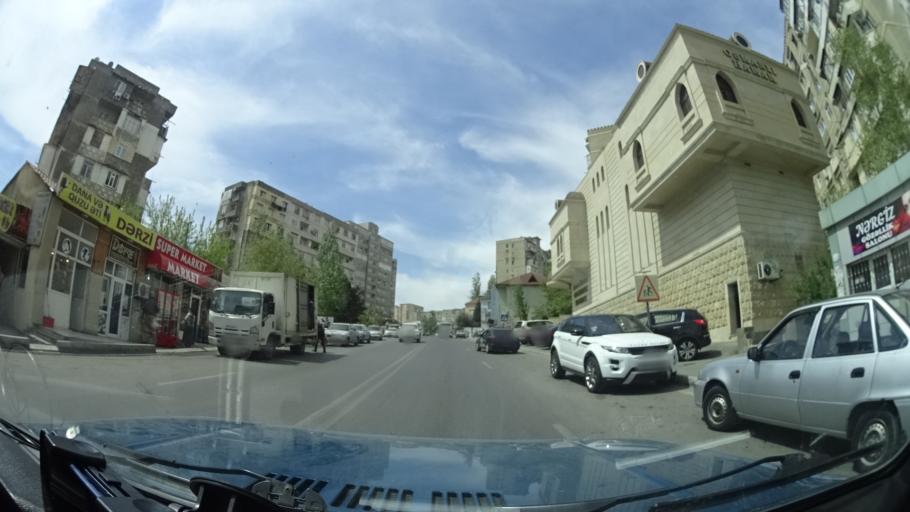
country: AZ
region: Baki
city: Khodzhi-Gasan
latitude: 40.3934
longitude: 49.7928
